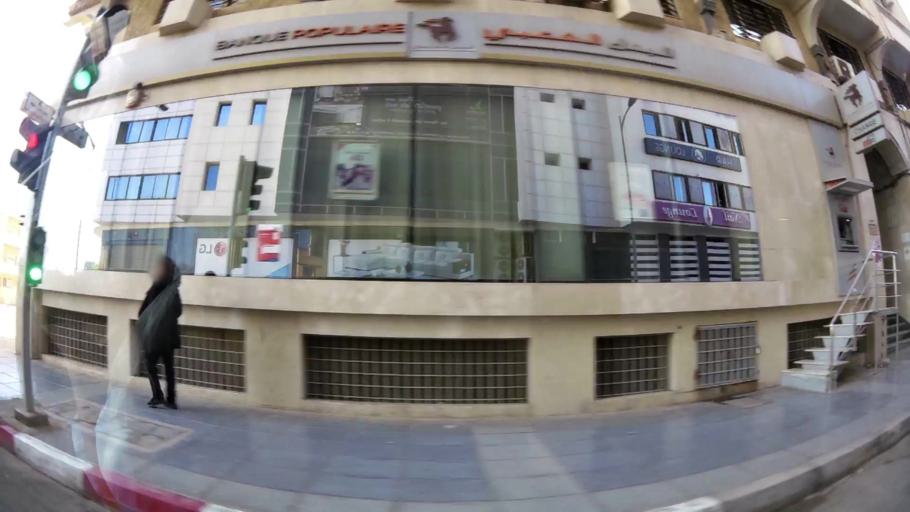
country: MA
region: Oriental
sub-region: Oujda-Angad
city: Oujda
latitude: 34.6898
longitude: -1.9173
